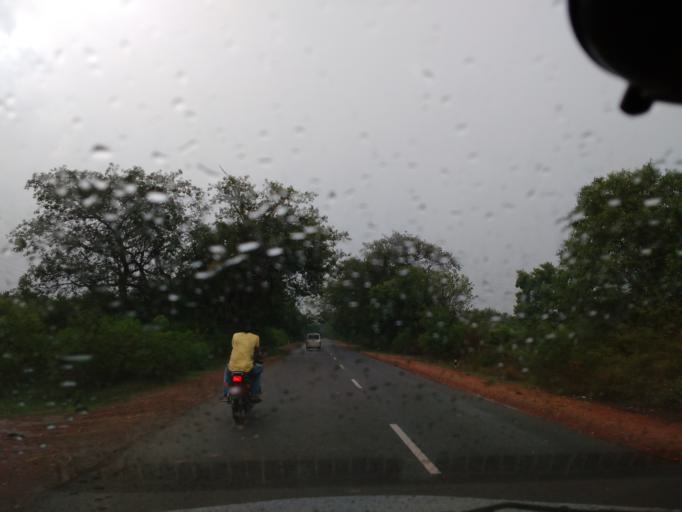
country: IN
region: Karnataka
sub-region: Tumkur
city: Chiknayakanhalli
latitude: 13.3043
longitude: 76.5986
